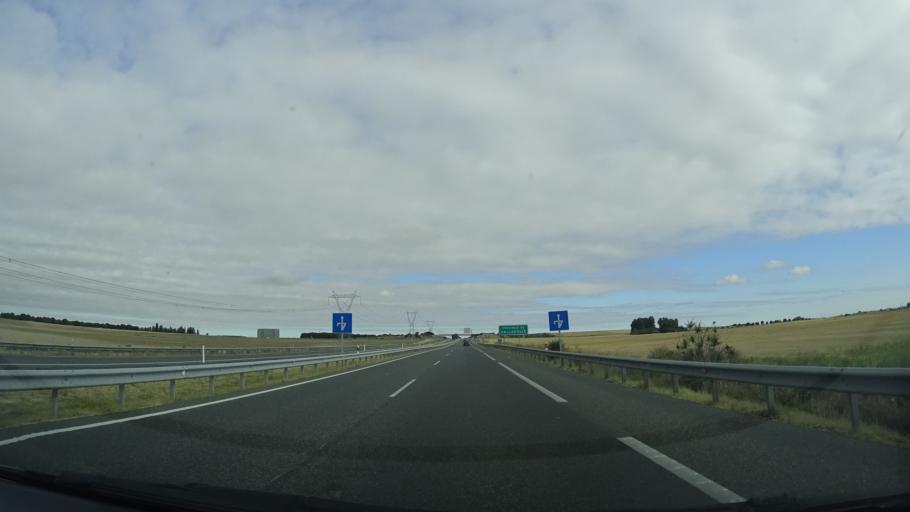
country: ES
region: Castille and Leon
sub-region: Provincia de Valladolid
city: San Pablo de la Moraleja
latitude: 41.1428
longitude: -4.7839
